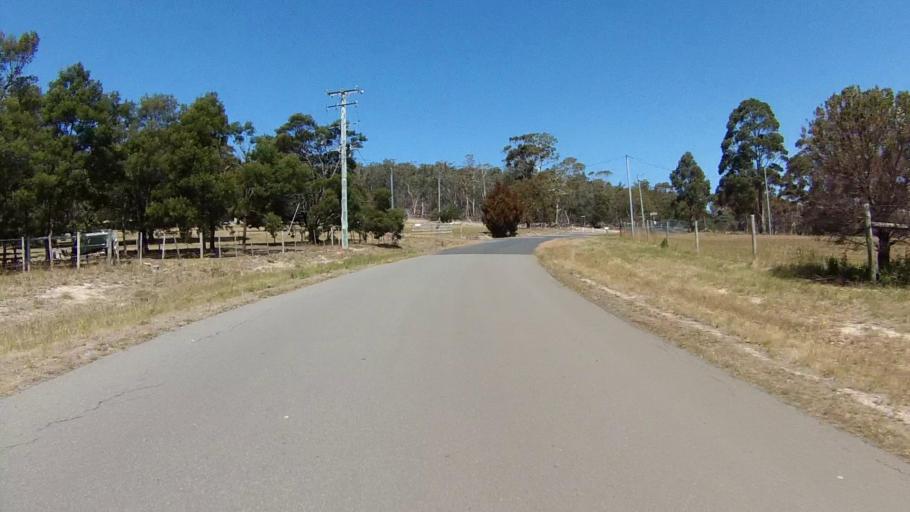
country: AU
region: Tasmania
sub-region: Clarence
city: Sandford
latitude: -42.9575
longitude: 147.4828
